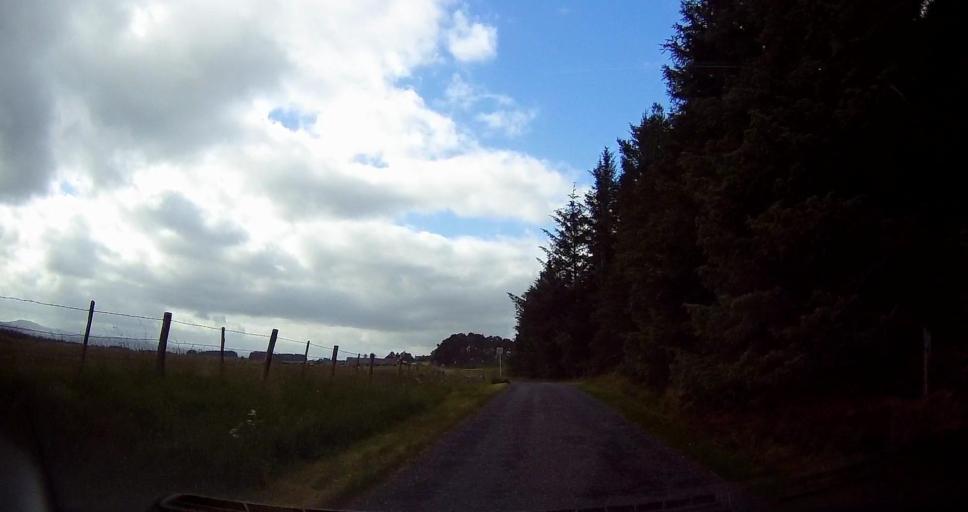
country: GB
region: Scotland
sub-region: Highland
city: Alness
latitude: 58.0688
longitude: -4.4278
